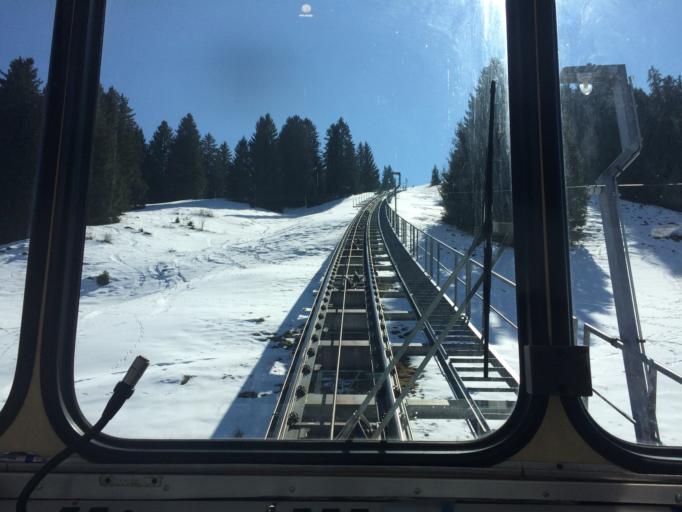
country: CH
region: Saint Gallen
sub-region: Wahlkreis Toggenburg
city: Wildhaus
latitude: 47.1915
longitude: 9.3117
